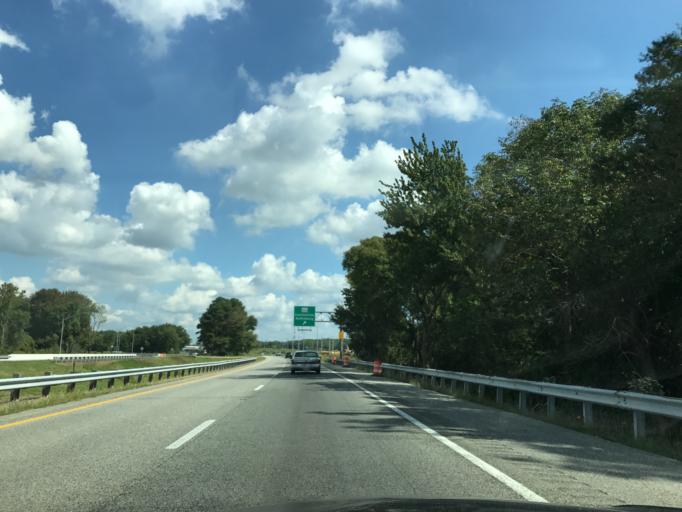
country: US
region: Maryland
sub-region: Queen Anne's County
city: Centreville
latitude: 39.0228
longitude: -76.0322
